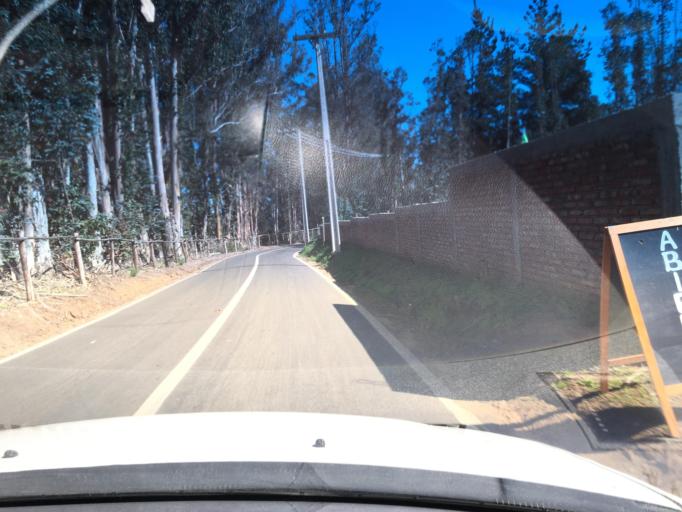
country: CL
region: Valparaiso
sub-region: San Antonio Province
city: El Tabo
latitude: -33.4155
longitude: -71.6192
